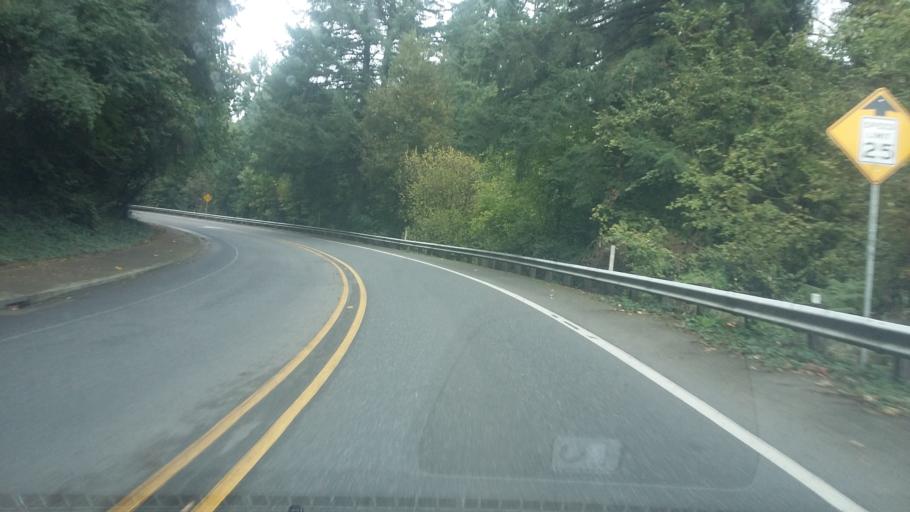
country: US
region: Washington
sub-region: Clark County
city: Ridgefield
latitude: 45.8158
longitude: -122.7345
